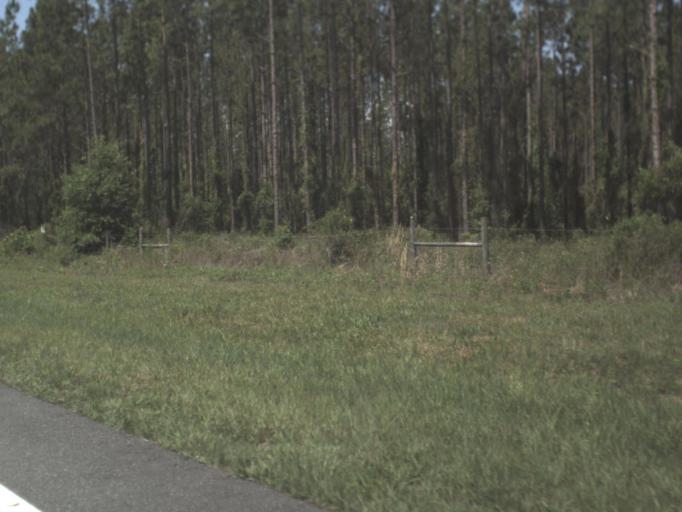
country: US
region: Florida
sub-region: Levy County
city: Williston
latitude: 29.4387
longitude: -82.4119
